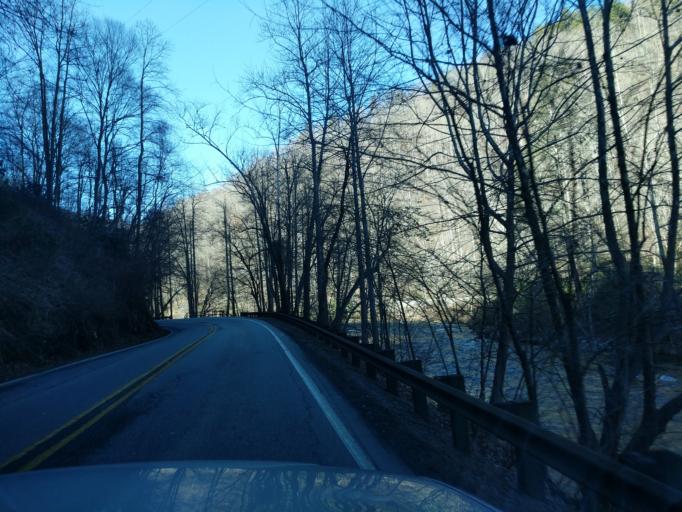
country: US
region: North Carolina
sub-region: Swain County
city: Bryson City
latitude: 35.3312
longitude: -83.6014
